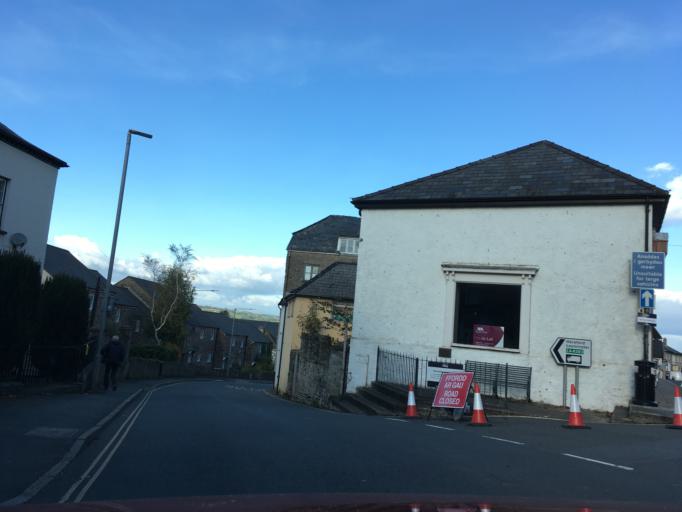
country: GB
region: Wales
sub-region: Sir Powys
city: Hay
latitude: 52.0737
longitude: -3.1275
